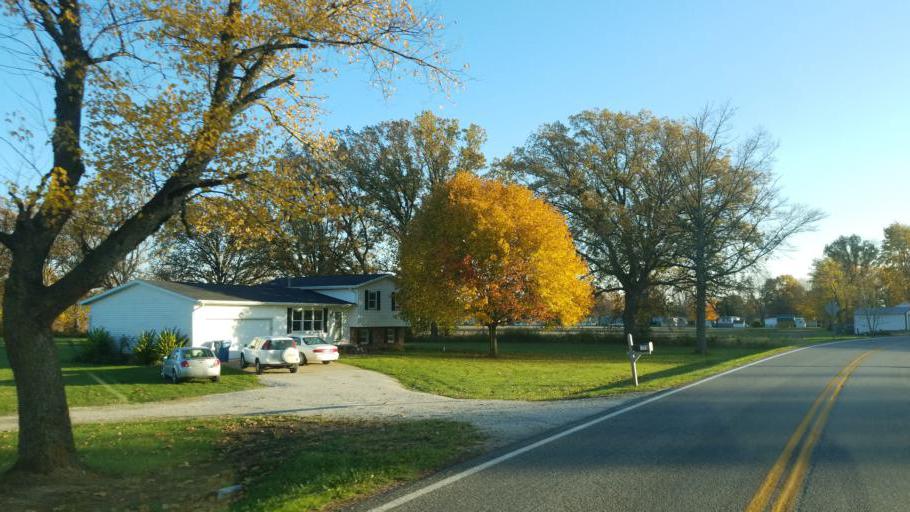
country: US
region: Ohio
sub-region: Sandusky County
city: Green Springs
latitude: 41.3292
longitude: -83.0517
